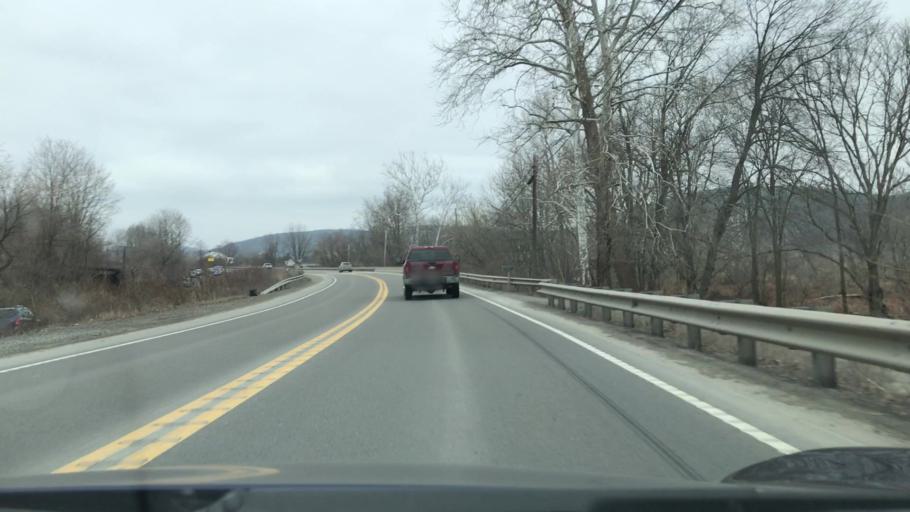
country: US
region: Pennsylvania
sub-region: Bradford County
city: Towanda
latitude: 41.7785
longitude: -76.3843
